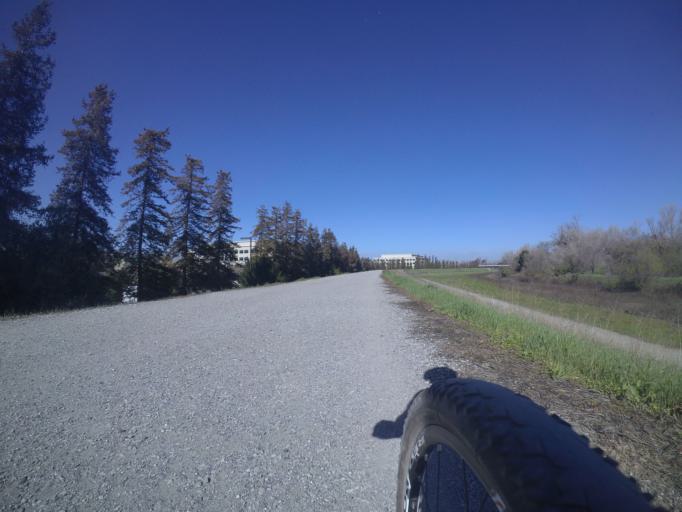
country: US
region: California
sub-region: Santa Clara County
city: Milpitas
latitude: 37.4058
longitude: -121.9247
